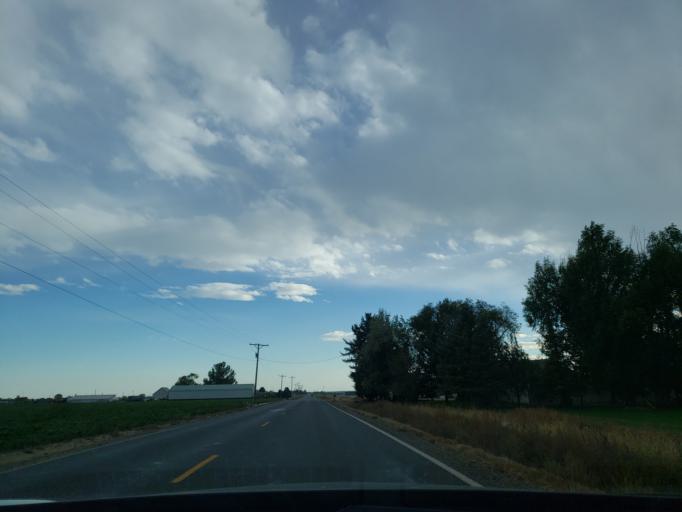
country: US
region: Colorado
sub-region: Larimer County
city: Wellington
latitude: 40.6358
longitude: -105.0197
